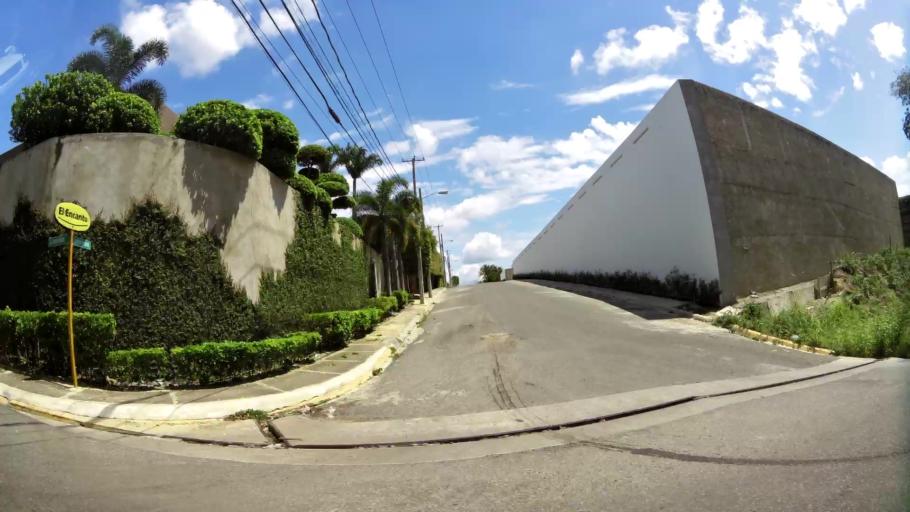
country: DO
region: Santiago
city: Santiago de los Caballeros
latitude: 19.4661
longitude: -70.6804
